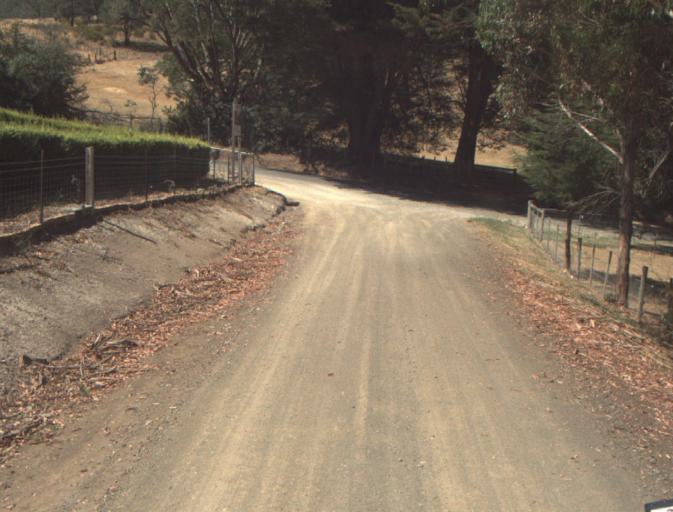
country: AU
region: Tasmania
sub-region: Launceston
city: Mayfield
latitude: -41.2578
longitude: 147.1879
